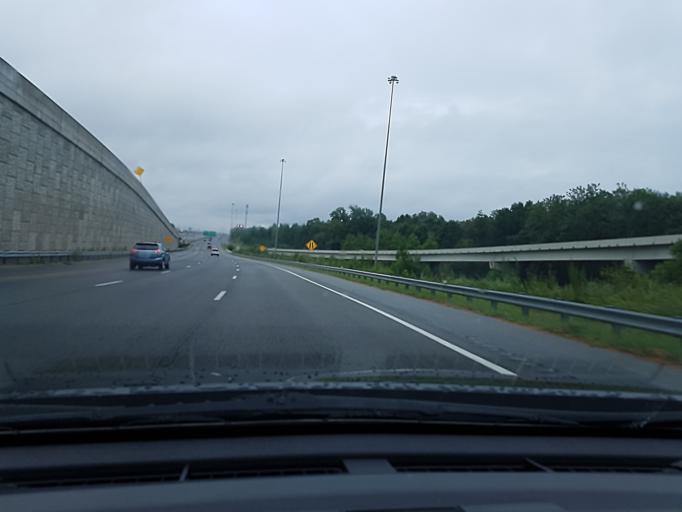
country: US
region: Georgia
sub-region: Gwinnett County
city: Duluth
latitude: 33.9650
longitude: -84.1031
